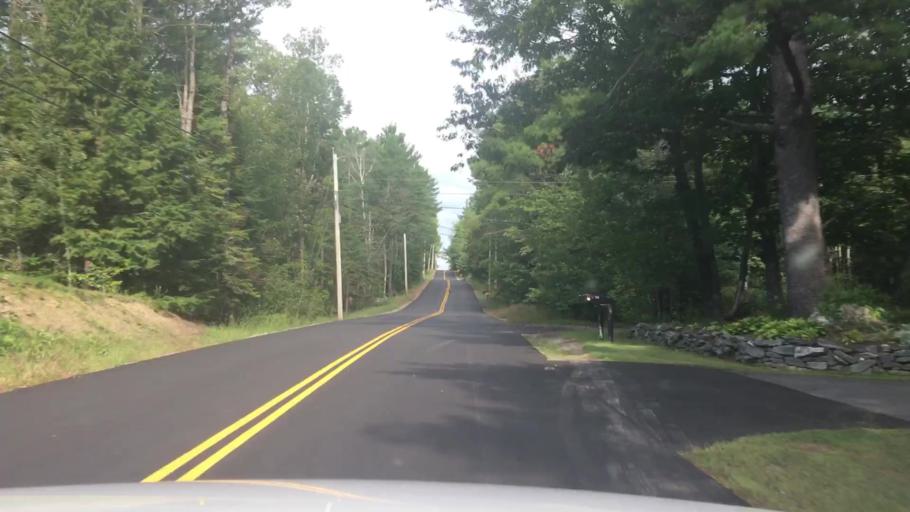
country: US
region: Maine
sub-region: Androscoggin County
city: Lisbon
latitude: 44.0544
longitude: -70.0745
